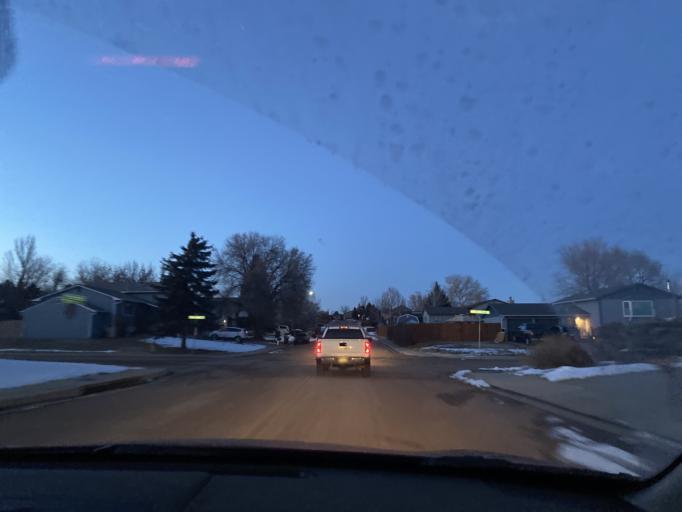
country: US
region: Colorado
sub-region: El Paso County
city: Security-Widefield
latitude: 38.7308
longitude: -104.6846
